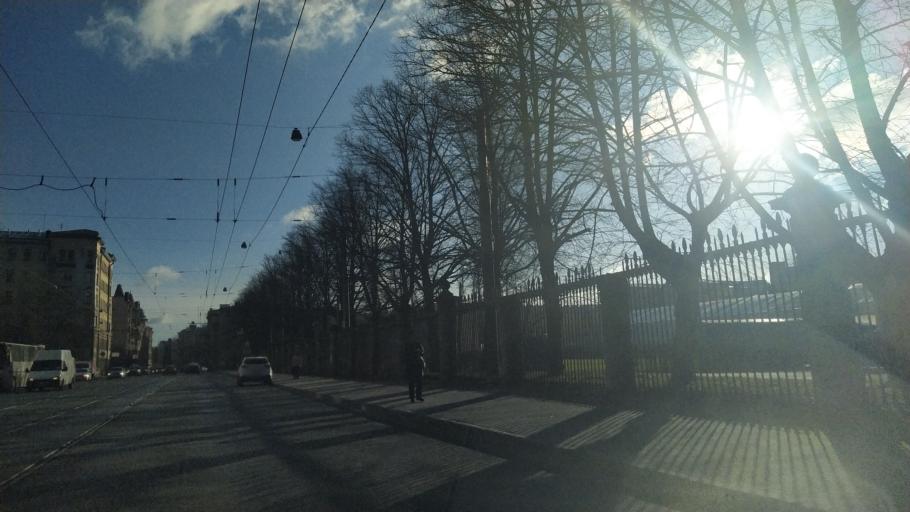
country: RU
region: Leningrad
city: Finlyandskiy
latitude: 59.9652
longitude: 30.3509
